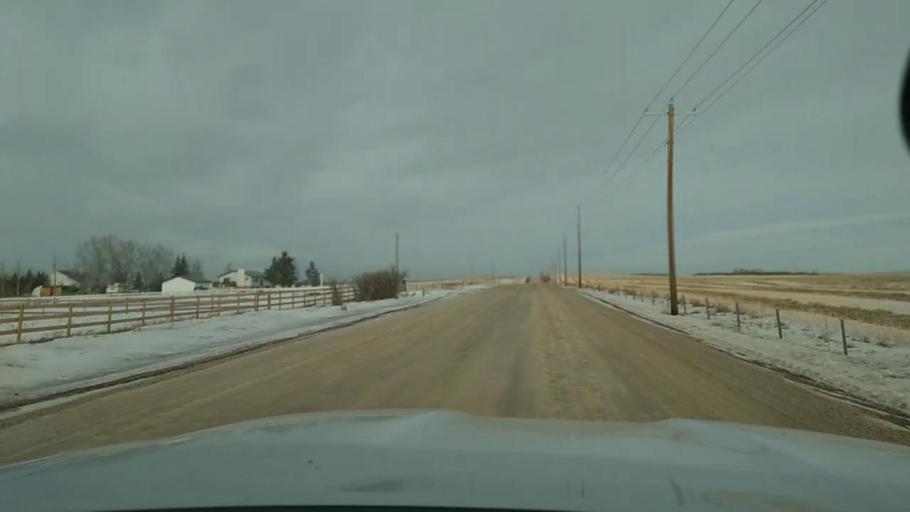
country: CA
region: Alberta
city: Airdrie
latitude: 51.2314
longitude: -113.9118
